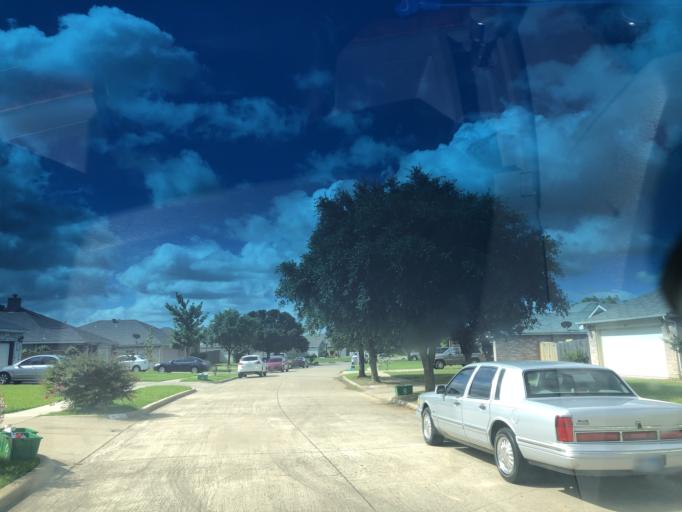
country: US
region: Texas
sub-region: Dallas County
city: Grand Prairie
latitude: 32.6952
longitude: -97.0315
